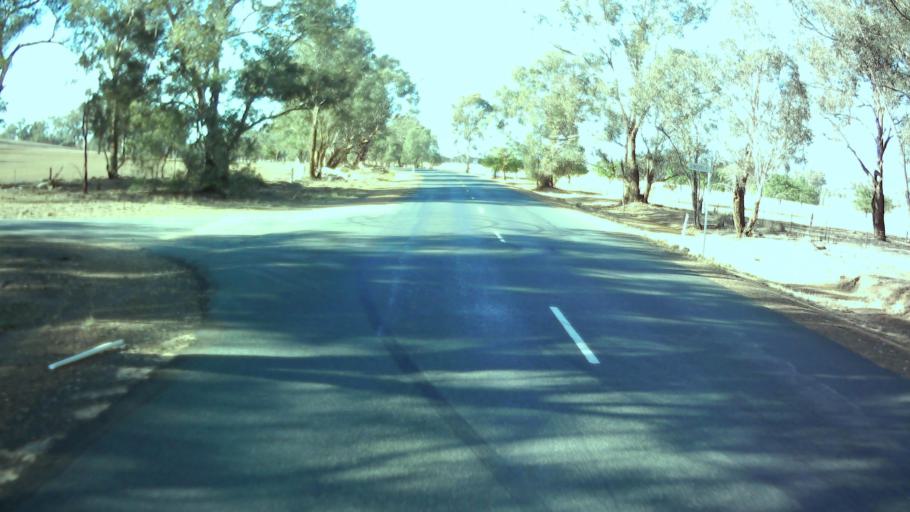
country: AU
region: New South Wales
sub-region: Weddin
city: Grenfell
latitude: -33.9417
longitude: 148.1361
